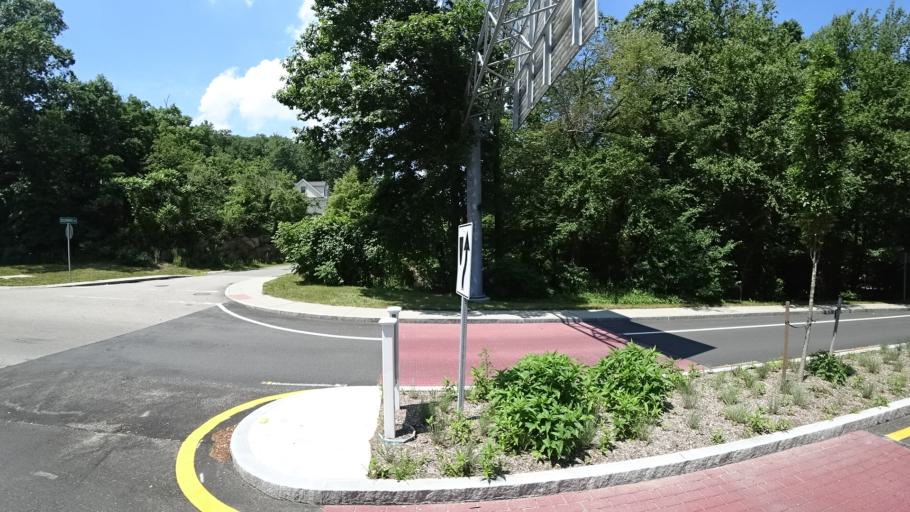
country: US
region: Massachusetts
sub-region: Norfolk County
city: Dedham
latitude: 42.2459
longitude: -71.1975
